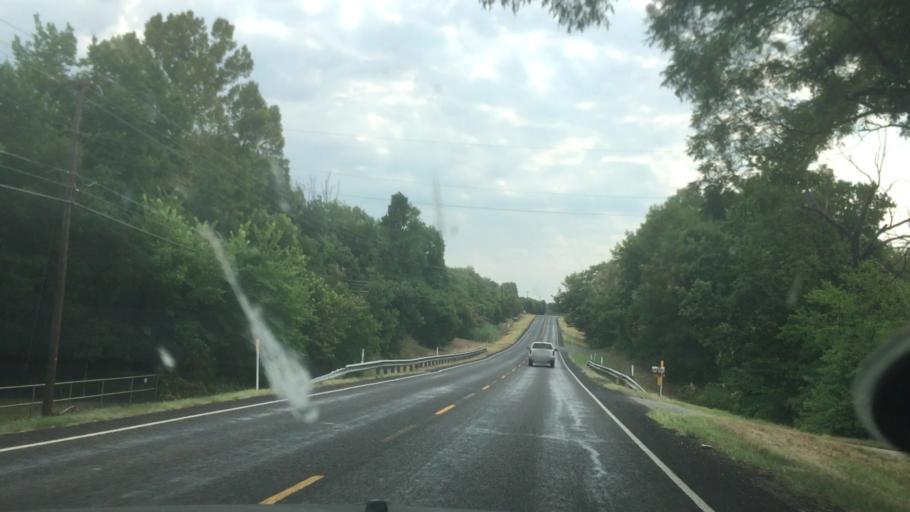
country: US
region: Texas
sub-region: Grayson County
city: Denison
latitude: 33.7843
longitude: -96.5945
